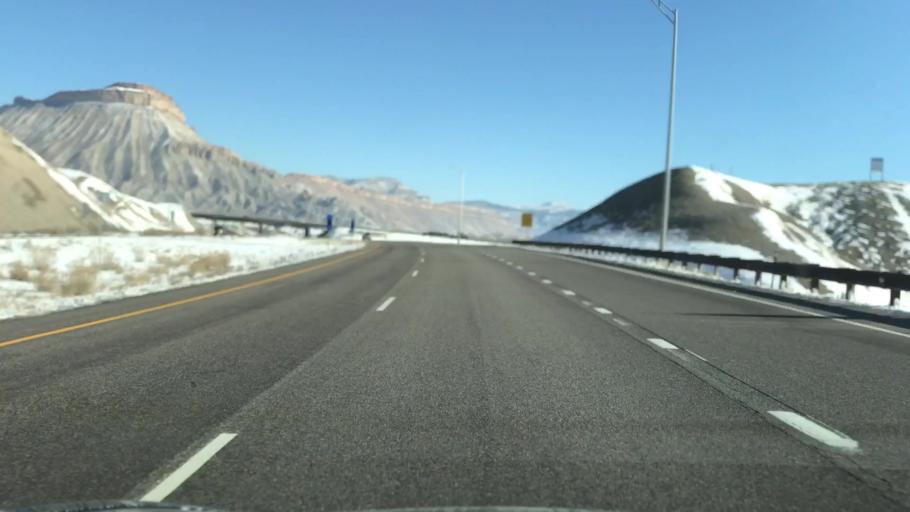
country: US
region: Colorado
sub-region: Mesa County
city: Clifton
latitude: 39.1022
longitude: -108.4516
